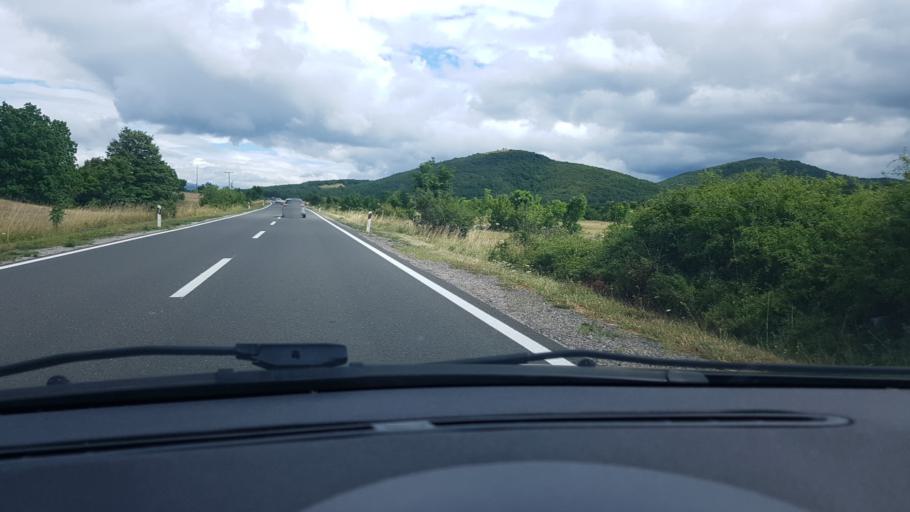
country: HR
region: Zadarska
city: Gracac
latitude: 44.4645
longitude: 15.8032
